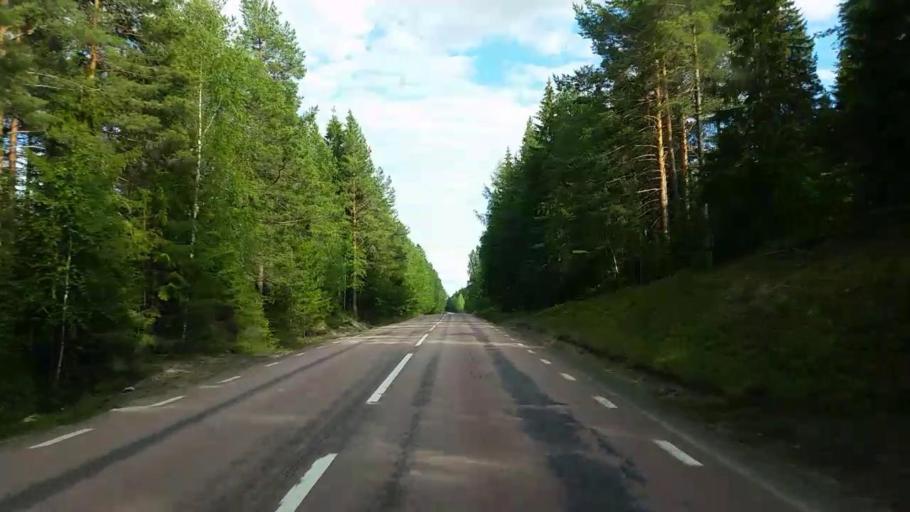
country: SE
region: Gaevleborg
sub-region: Ljusdals Kommun
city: Farila
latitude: 61.8821
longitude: 15.9406
